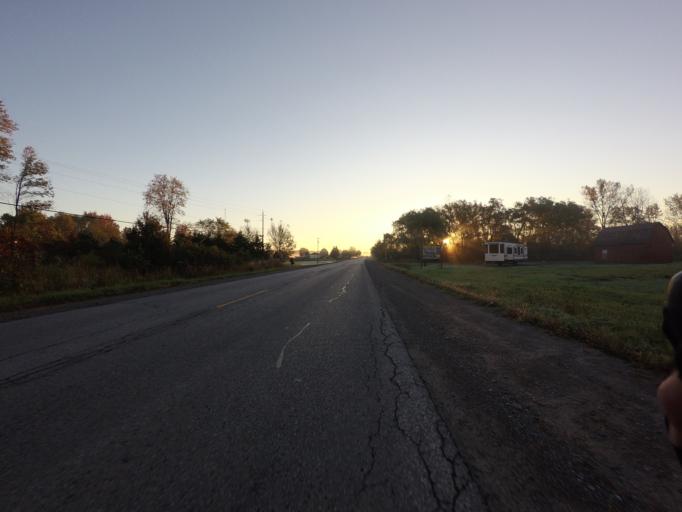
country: CA
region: Ontario
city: Quinte West
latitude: 44.0402
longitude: -77.6278
